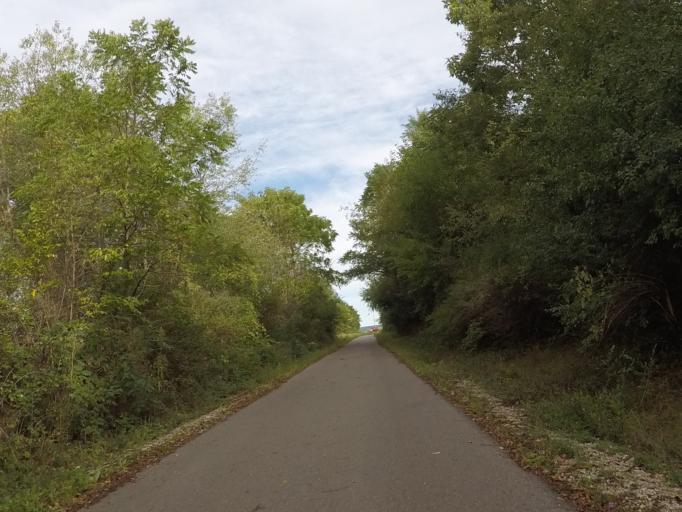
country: US
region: Wisconsin
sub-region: Sauk County
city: Prairie du Sac
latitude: 43.3124
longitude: -89.7340
